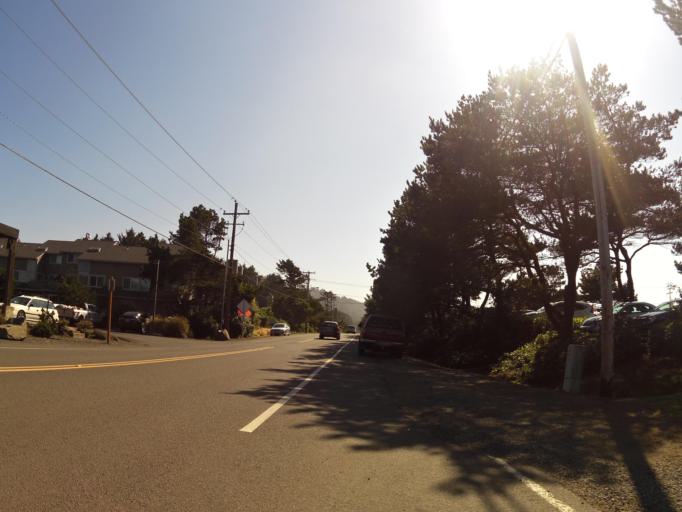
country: US
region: Oregon
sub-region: Clatsop County
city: Cannon Beach
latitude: 45.8720
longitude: -123.9599
